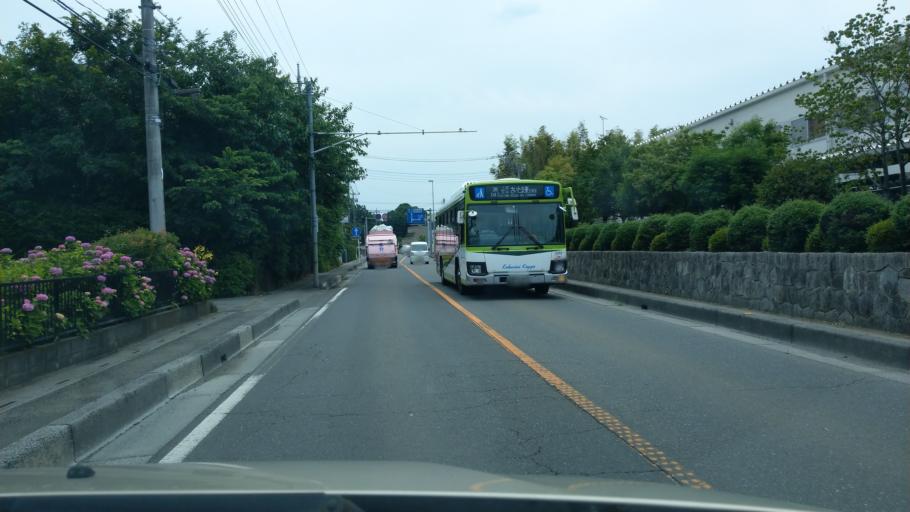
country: JP
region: Saitama
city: Saitama
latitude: 35.9105
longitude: 139.6953
